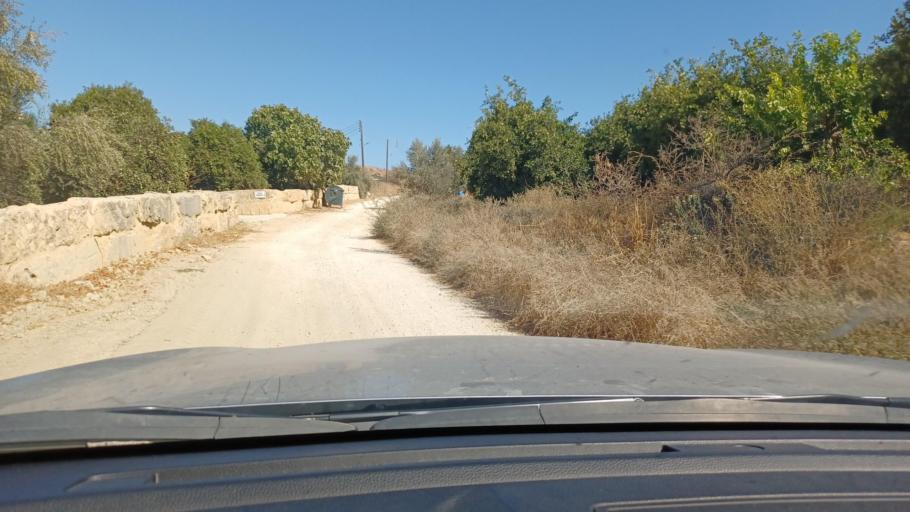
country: CY
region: Pafos
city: Polis
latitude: 35.0236
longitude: 32.4503
